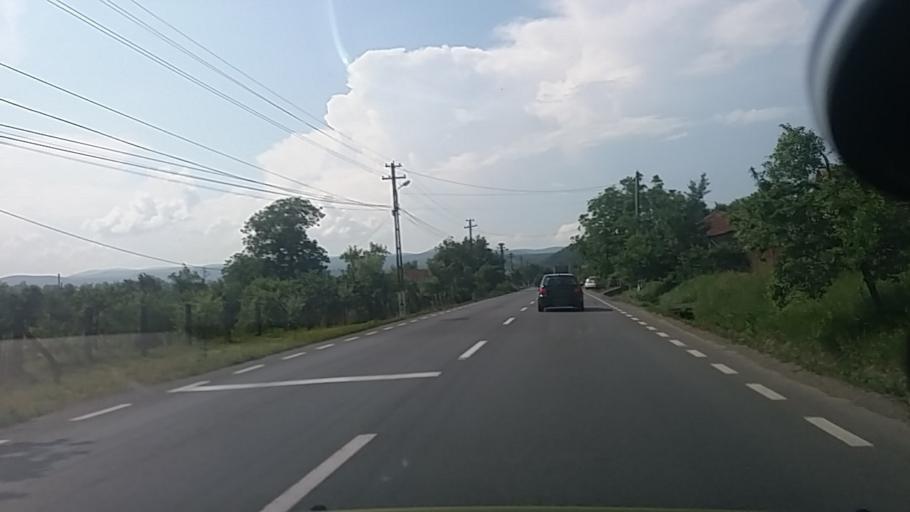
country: RO
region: Arad
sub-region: Comuna Barzava
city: Barzava
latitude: 46.0902
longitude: 22.0233
